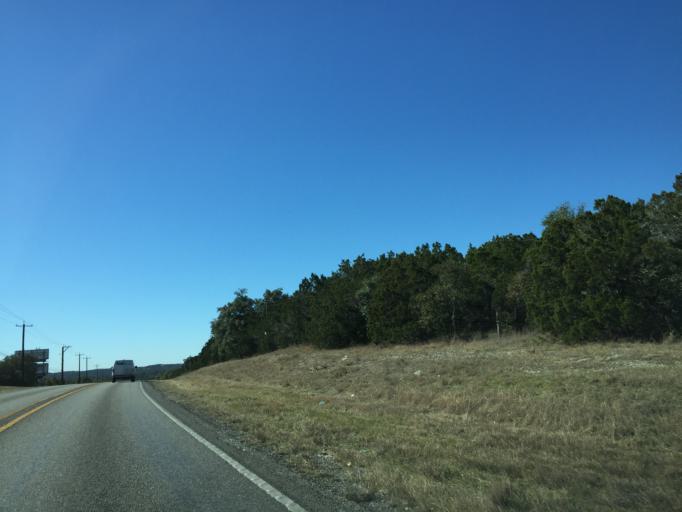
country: US
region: Texas
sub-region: Comal County
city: Garden Ridge
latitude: 29.7099
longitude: -98.3102
